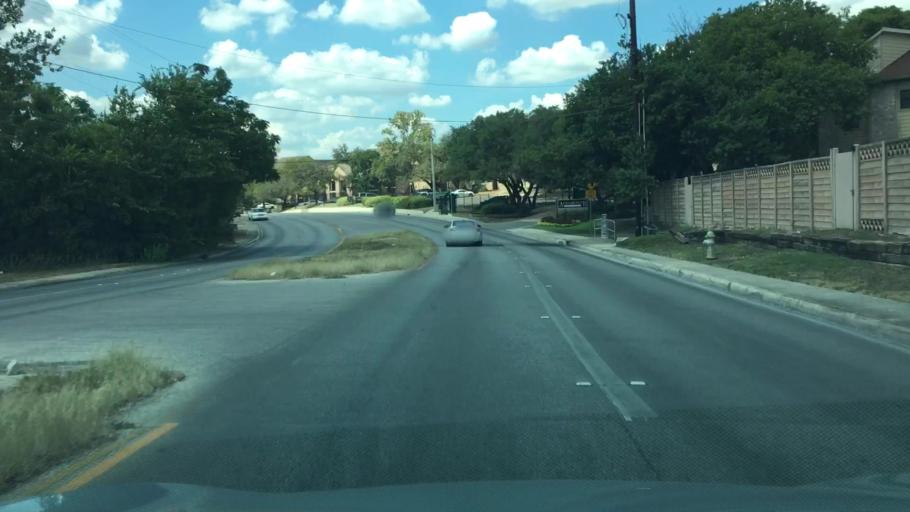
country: US
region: Texas
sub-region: Bexar County
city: Hollywood Park
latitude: 29.5560
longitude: -98.4719
